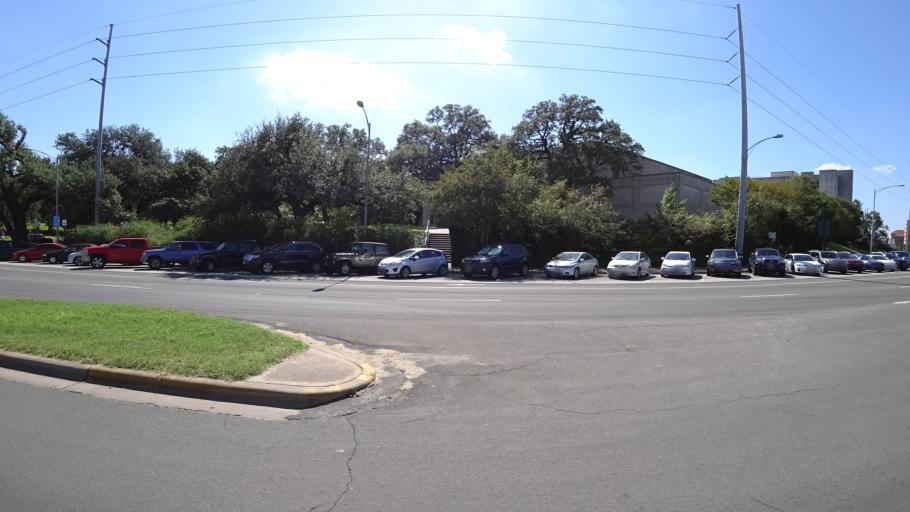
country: US
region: Texas
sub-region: Travis County
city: Austin
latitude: 30.2888
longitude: -97.7296
